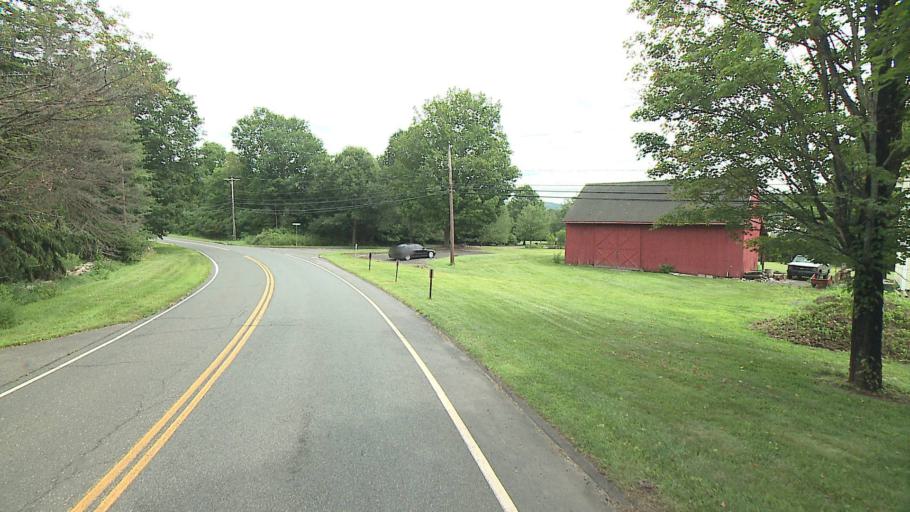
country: US
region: Connecticut
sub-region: Litchfield County
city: Woodbury
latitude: 41.5407
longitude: -73.2316
